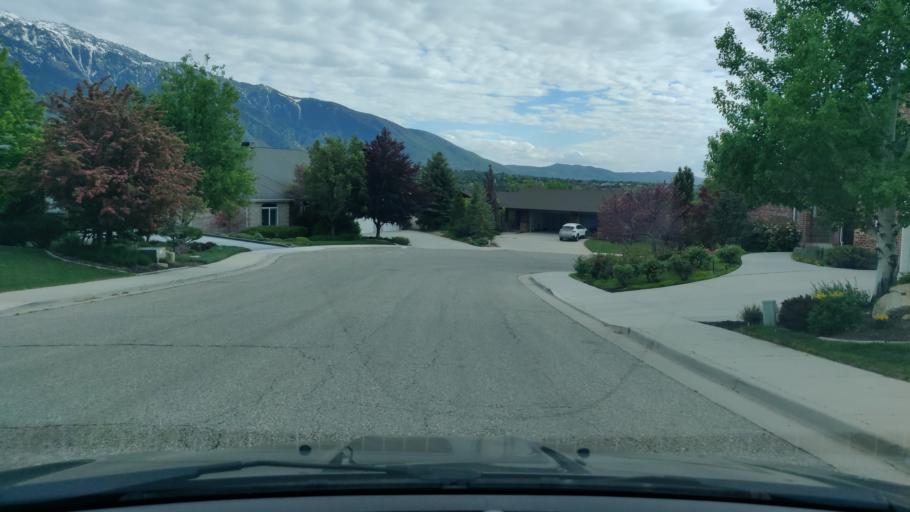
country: US
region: Utah
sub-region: Salt Lake County
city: Cottonwood Heights
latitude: 40.6073
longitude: -111.8137
